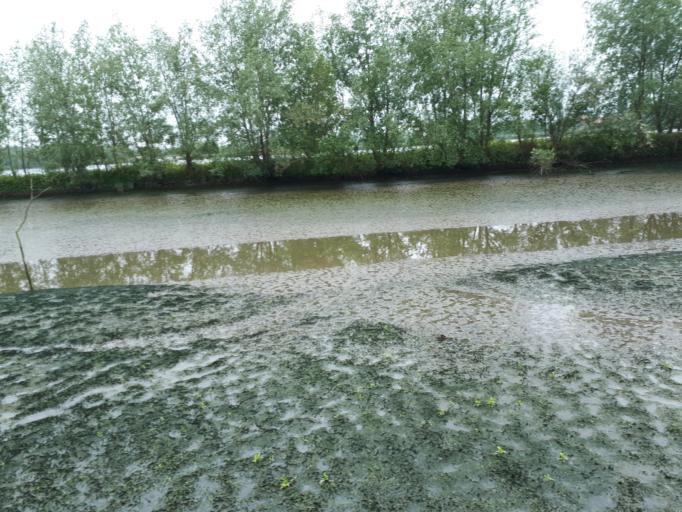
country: NL
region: South Holland
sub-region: Gemeente Albrandswaard
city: Rhoon
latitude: 51.8356
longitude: 4.4445
